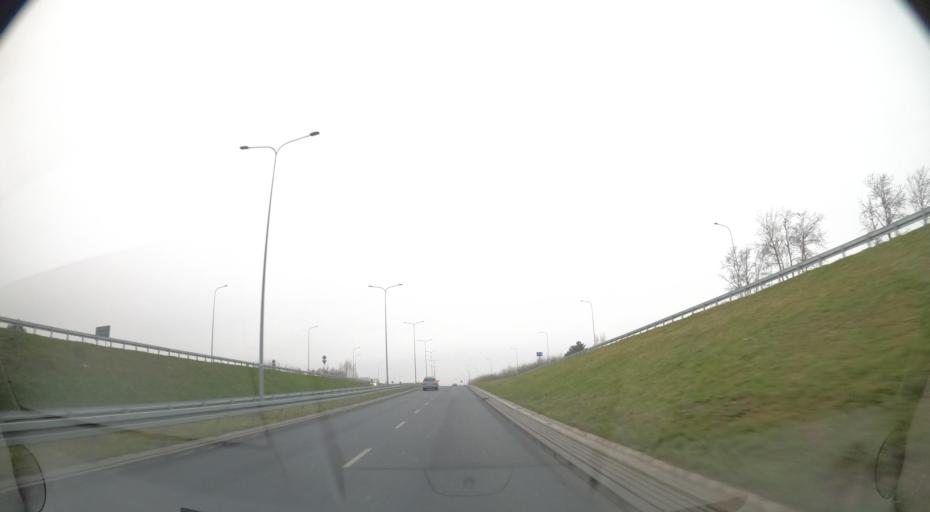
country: PL
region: Masovian Voivodeship
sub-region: Radom
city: Radom
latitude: 51.3962
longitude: 21.1968
